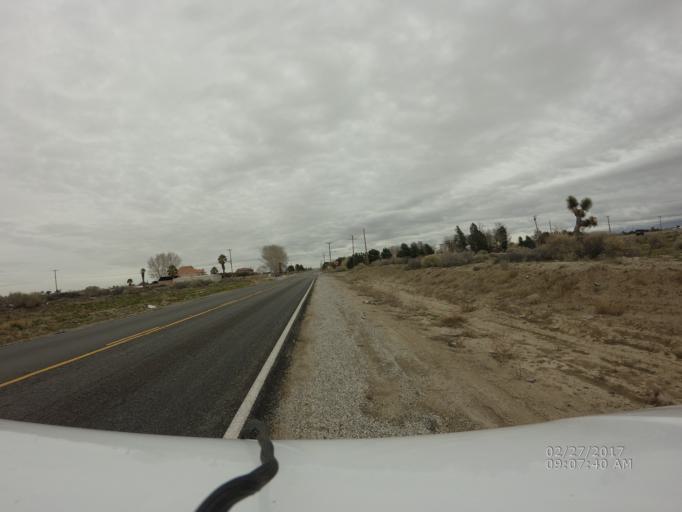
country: US
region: California
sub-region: Los Angeles County
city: Lancaster
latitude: 34.7189
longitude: -118.0780
